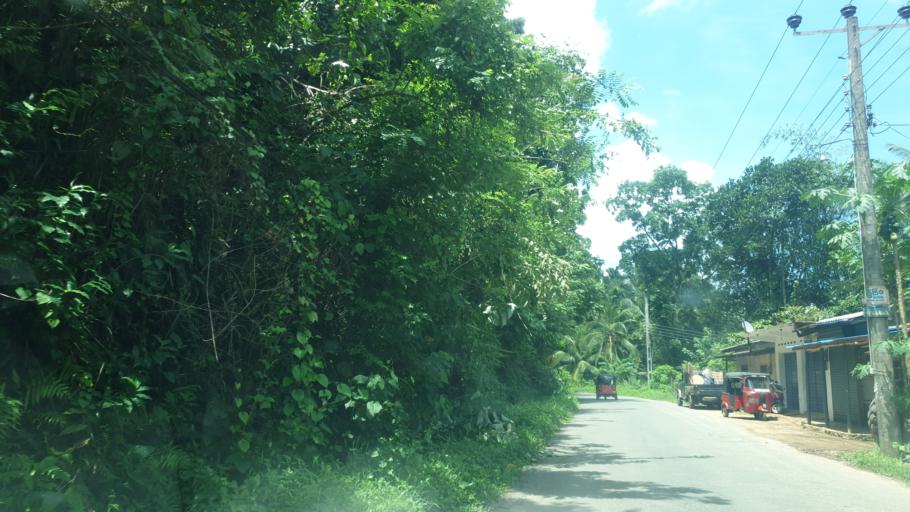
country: LK
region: Sabaragamuwa
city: Ratnapura
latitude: 6.4844
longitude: 80.4066
